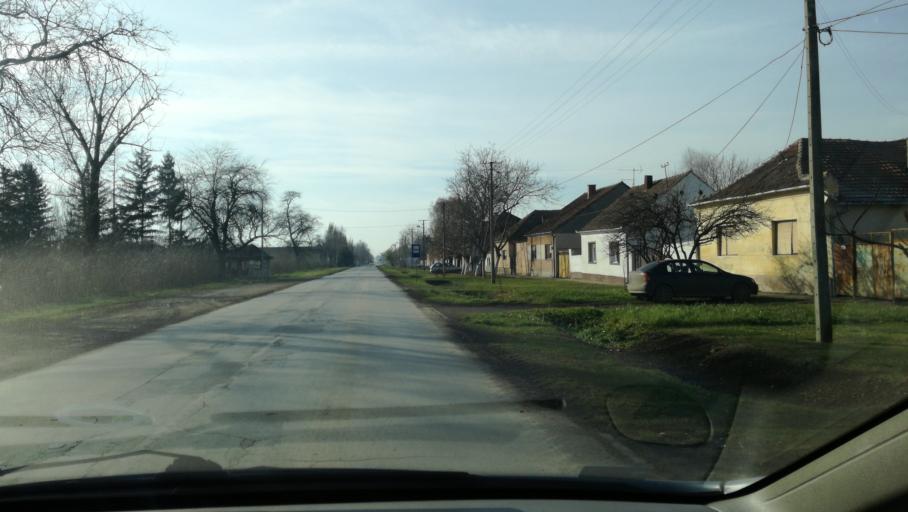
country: RS
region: Autonomna Pokrajina Vojvodina
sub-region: Severnobanatski Okrug
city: Kikinda
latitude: 45.8312
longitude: 20.4881
